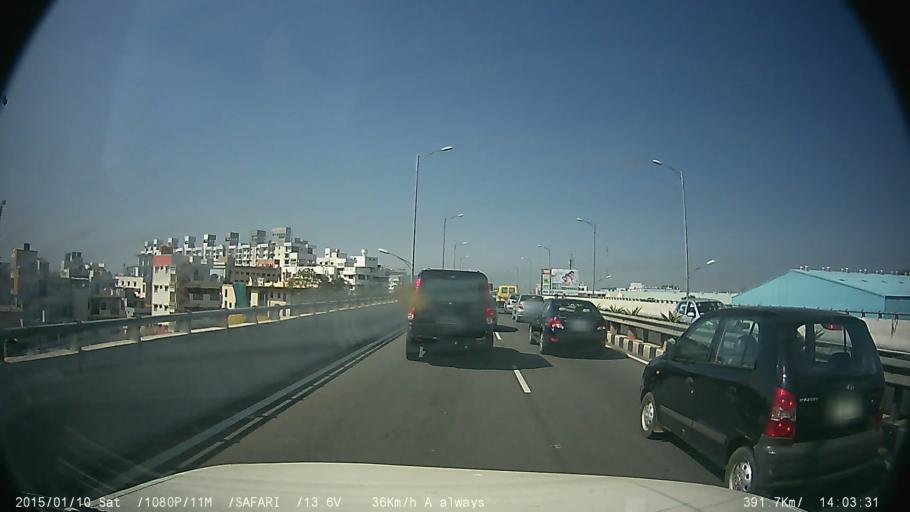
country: IN
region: Karnataka
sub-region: Bangalore Urban
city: Bangalore
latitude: 12.8874
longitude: 77.6408
